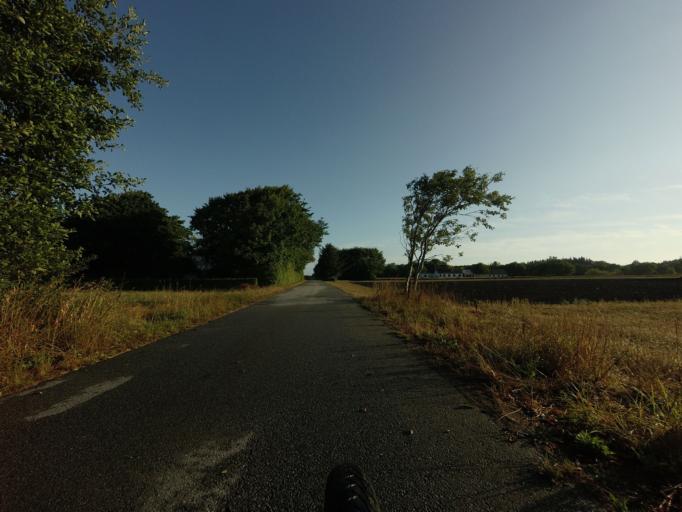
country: DK
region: North Denmark
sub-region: Hjorring Kommune
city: Vra
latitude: 57.3616
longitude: 9.8658
